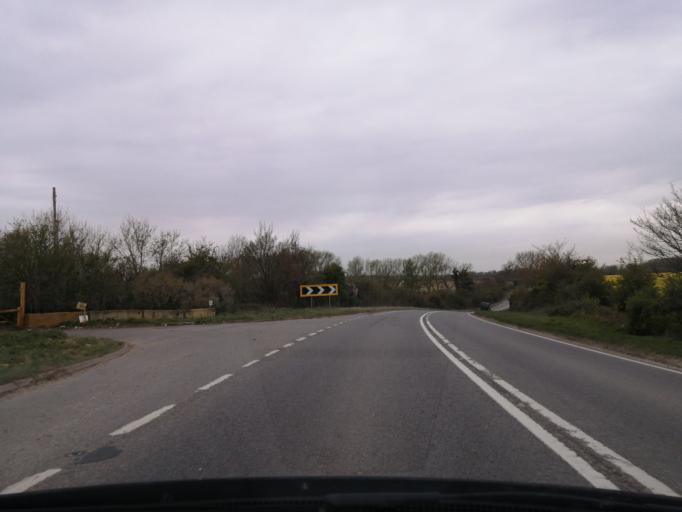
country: GB
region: England
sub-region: Peterborough
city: Thornhaugh
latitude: 52.5858
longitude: -0.4380
